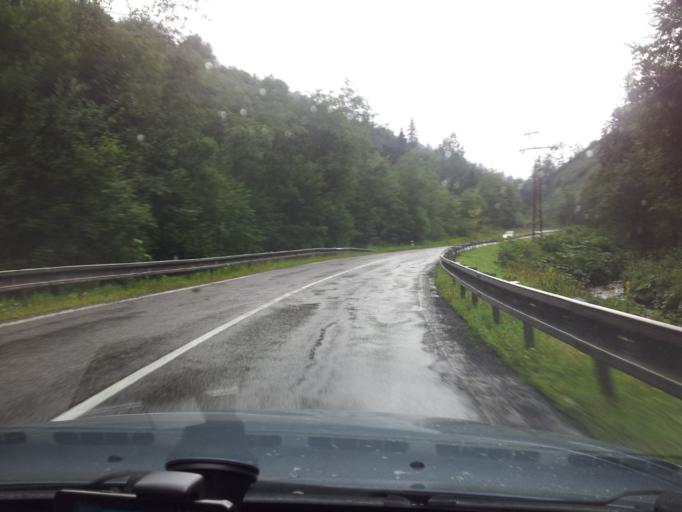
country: SK
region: Banskobystricky
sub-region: Okres Banska Bystrica
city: Brezno
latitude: 48.8852
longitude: 19.6668
